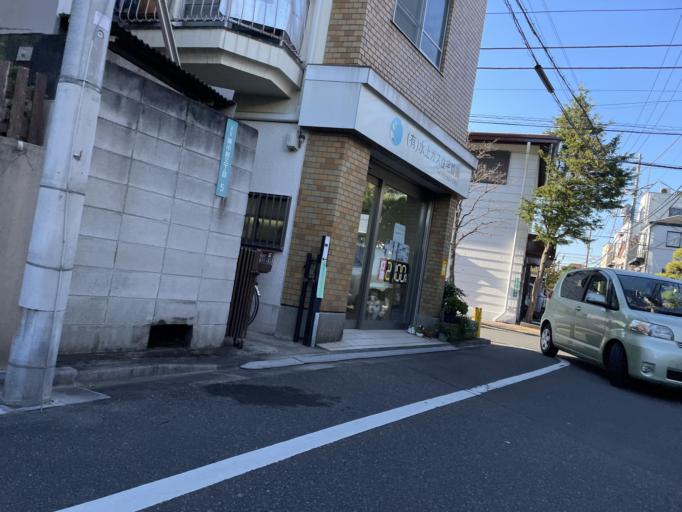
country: JP
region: Tokyo
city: Urayasu
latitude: 35.7252
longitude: 139.8850
